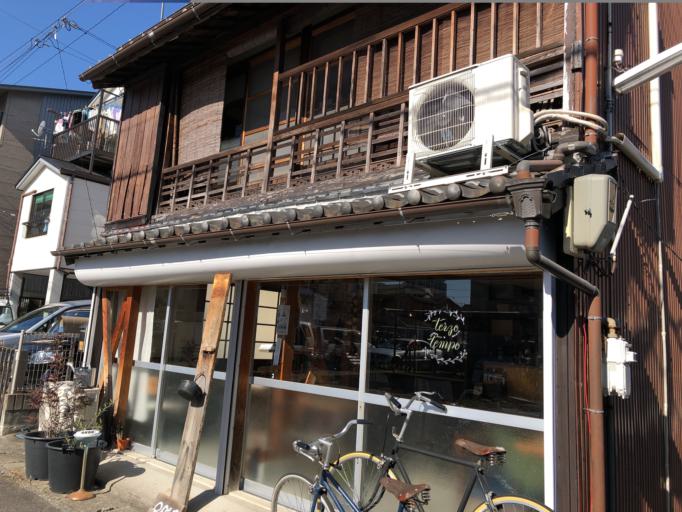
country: JP
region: Kochi
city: Kochi-shi
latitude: 33.5609
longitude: 133.5514
